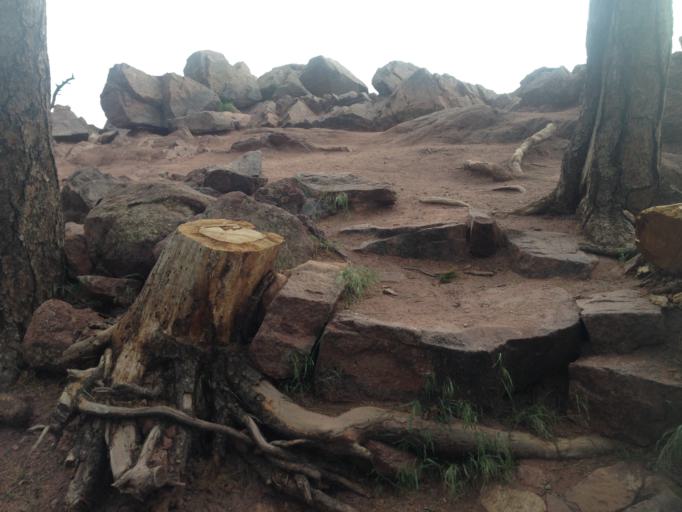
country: US
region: Colorado
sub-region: Boulder County
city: Boulder
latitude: 40.0343
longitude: -105.3054
